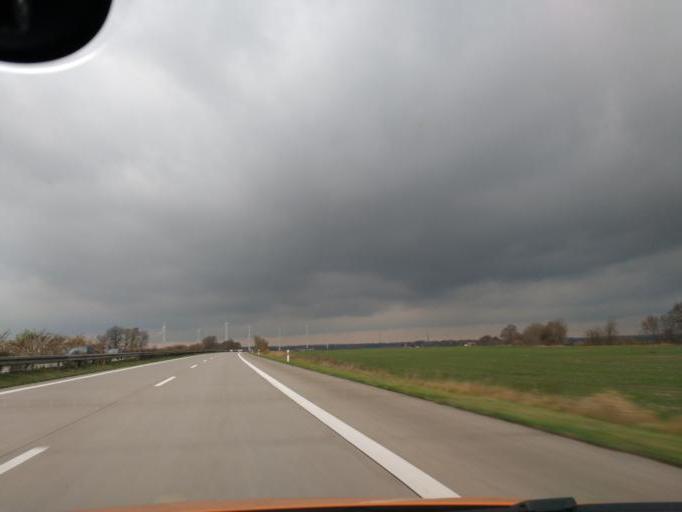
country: DE
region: Brandenburg
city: Heiligengrabe
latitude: 53.1737
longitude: 12.3219
